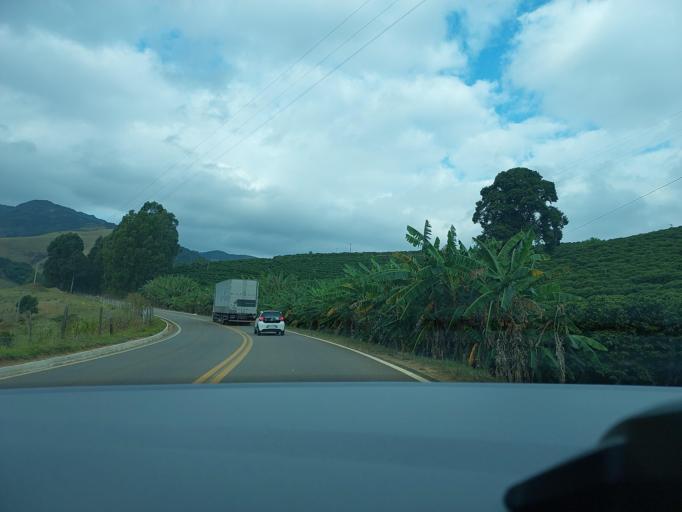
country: BR
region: Minas Gerais
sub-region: Visconde Do Rio Branco
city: Visconde do Rio Branco
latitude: -20.9522
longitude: -42.6094
